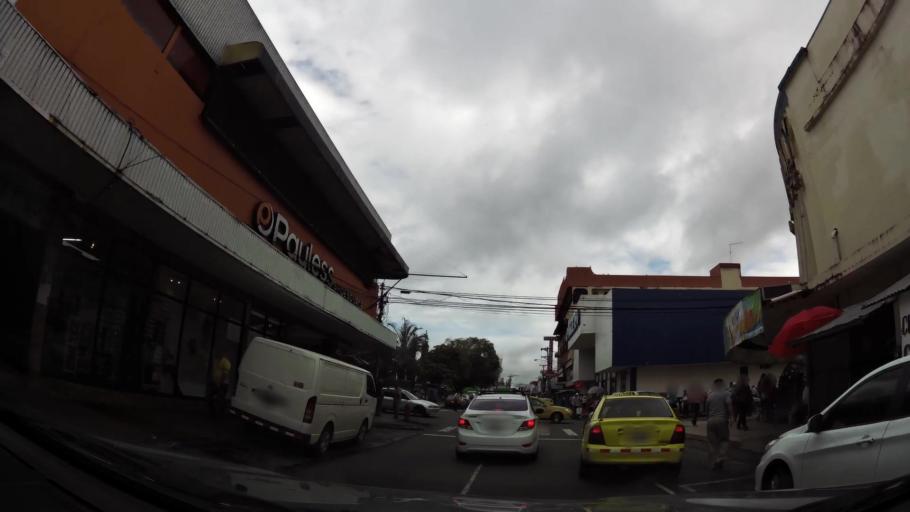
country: PA
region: Chiriqui
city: David
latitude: 8.4273
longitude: -82.4255
